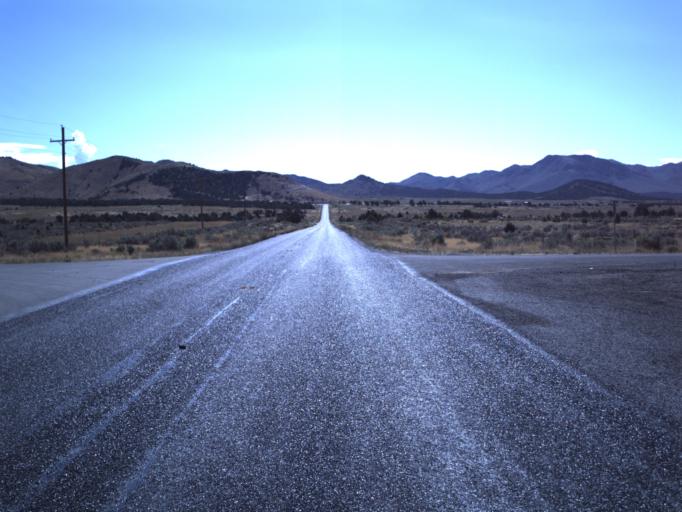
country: US
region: Utah
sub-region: Utah County
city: Genola
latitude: 39.9274
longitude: -112.1609
